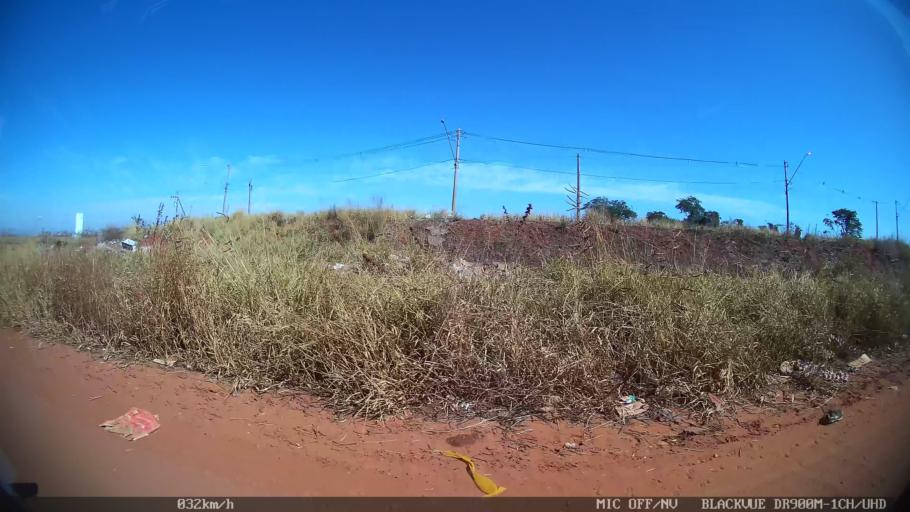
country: BR
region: Sao Paulo
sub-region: Sao Jose Do Rio Preto
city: Sao Jose do Rio Preto
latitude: -20.7437
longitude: -49.4340
